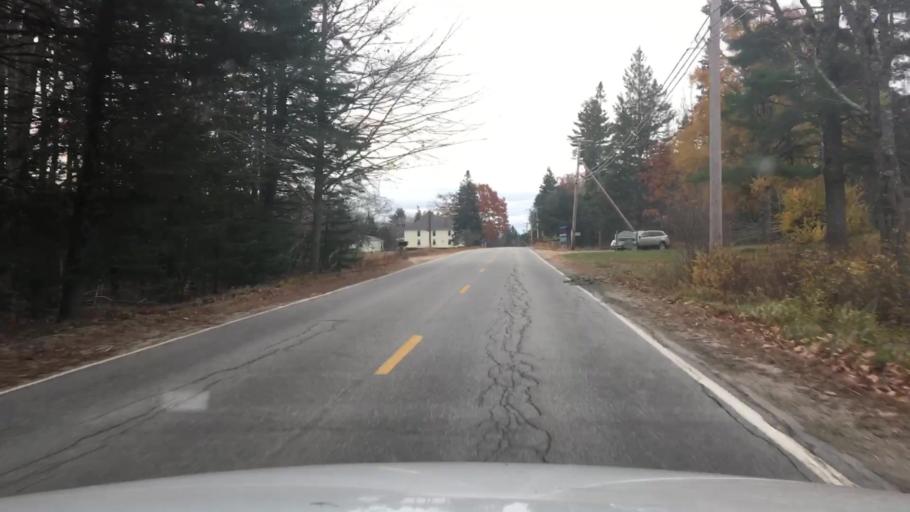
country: US
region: Maine
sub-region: Hancock County
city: Sedgwick
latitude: 44.3654
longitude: -68.5527
